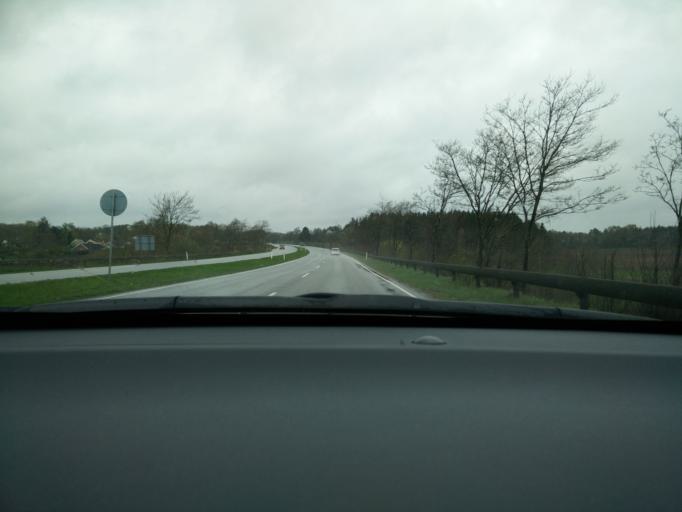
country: DK
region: Central Jutland
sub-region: Viborg Kommune
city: Viborg
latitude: 56.4044
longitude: 9.4338
